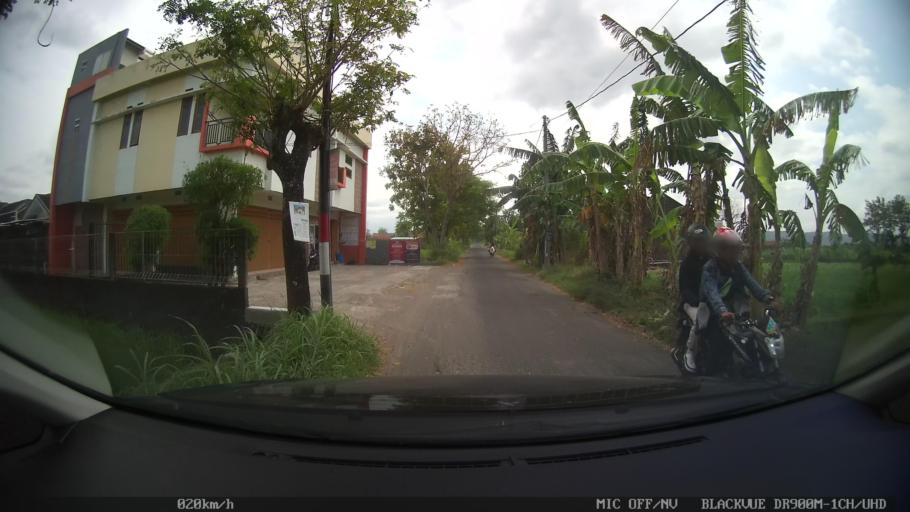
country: ID
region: Daerah Istimewa Yogyakarta
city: Depok
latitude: -7.8293
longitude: 110.4634
